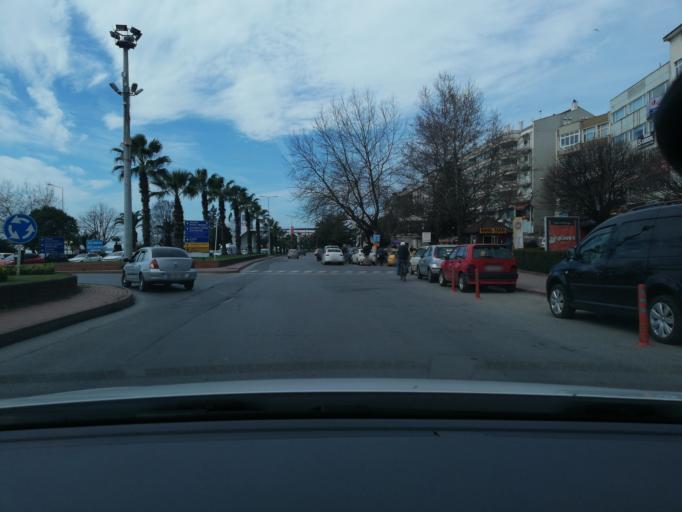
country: TR
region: Zonguldak
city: Eregli
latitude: 41.2800
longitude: 31.4202
